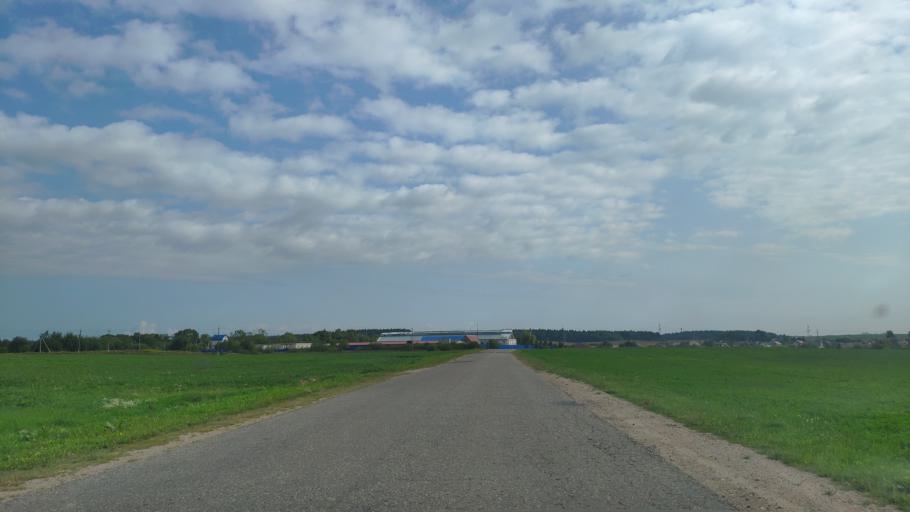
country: BY
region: Minsk
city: Khatsyezhyna
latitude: 53.8598
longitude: 27.3097
